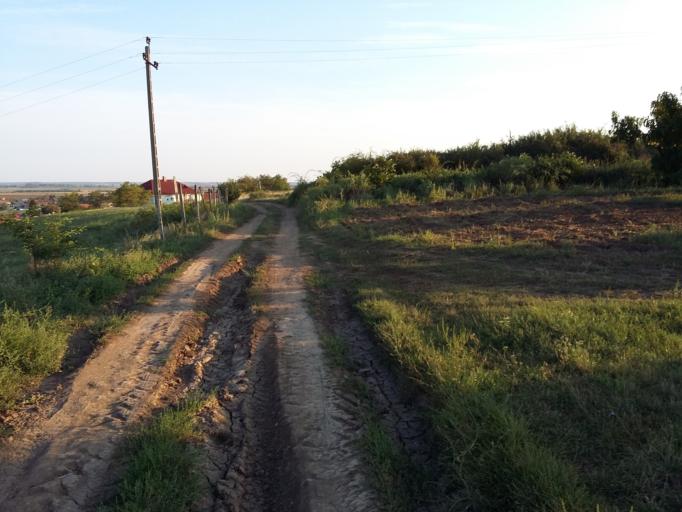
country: HU
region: Borsod-Abauj-Zemplen
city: Bekecs
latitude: 48.1598
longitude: 21.1769
